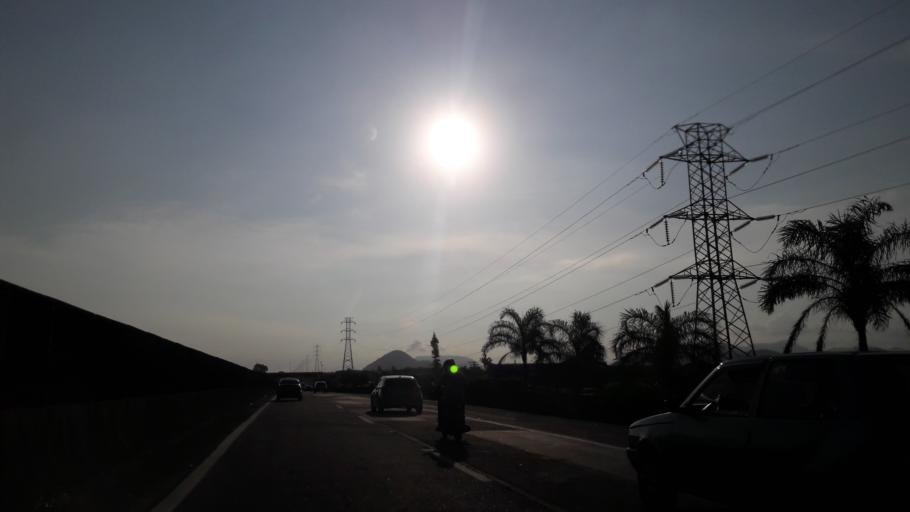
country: BR
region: Sao Paulo
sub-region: Mongagua
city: Mongagua
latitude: -24.1001
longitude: -46.6348
